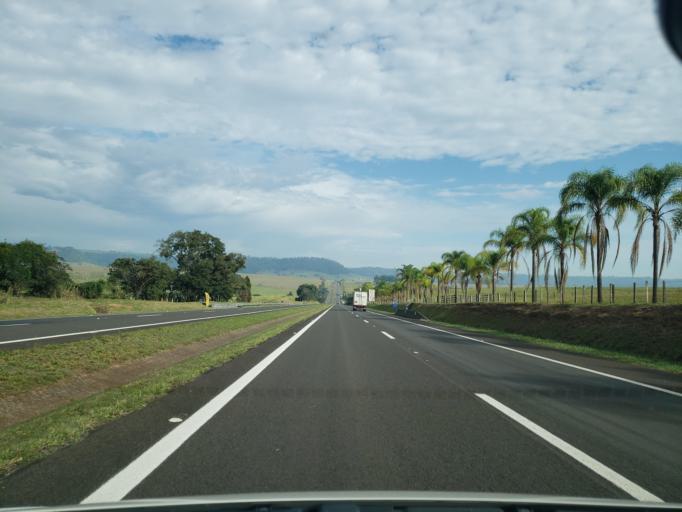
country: BR
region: Sao Paulo
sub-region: Dois Corregos
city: Dois Corregos
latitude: -22.2449
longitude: -48.3034
